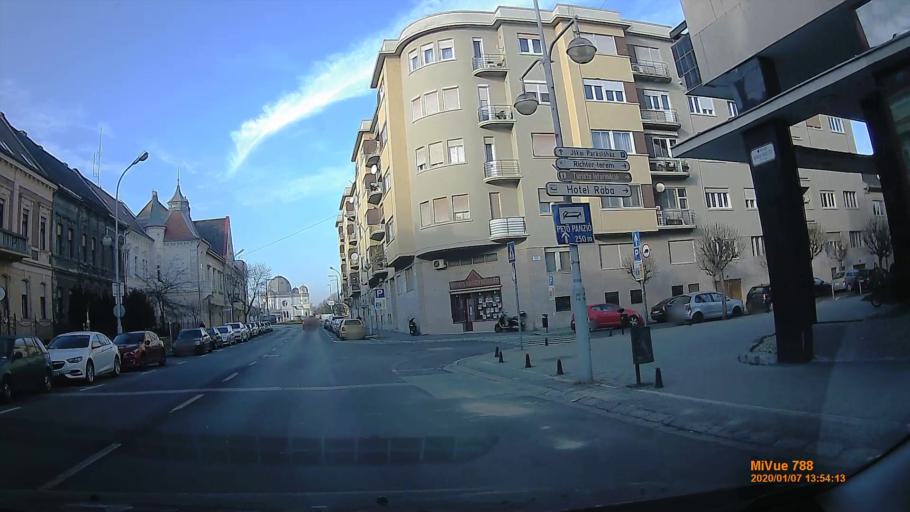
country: HU
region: Gyor-Moson-Sopron
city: Gyor
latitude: 47.6825
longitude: 17.6287
